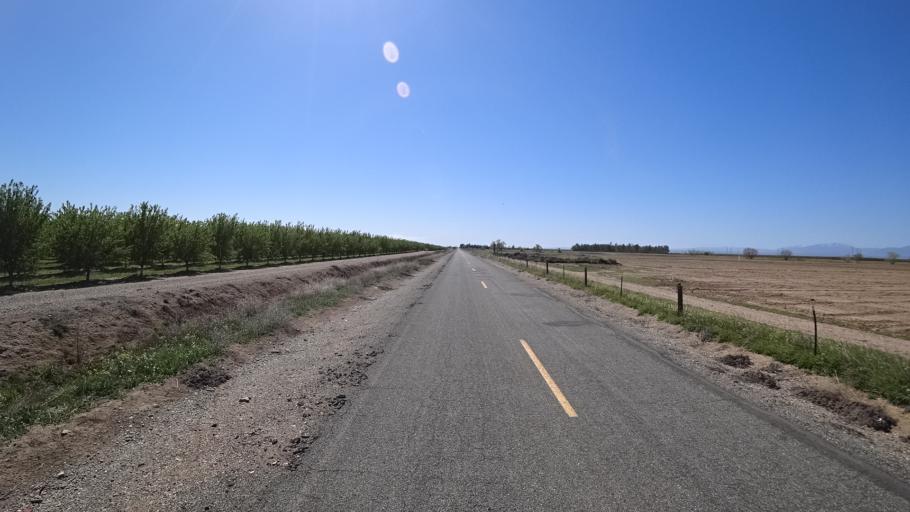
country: US
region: California
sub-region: Glenn County
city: Orland
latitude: 39.6917
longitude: -122.2530
